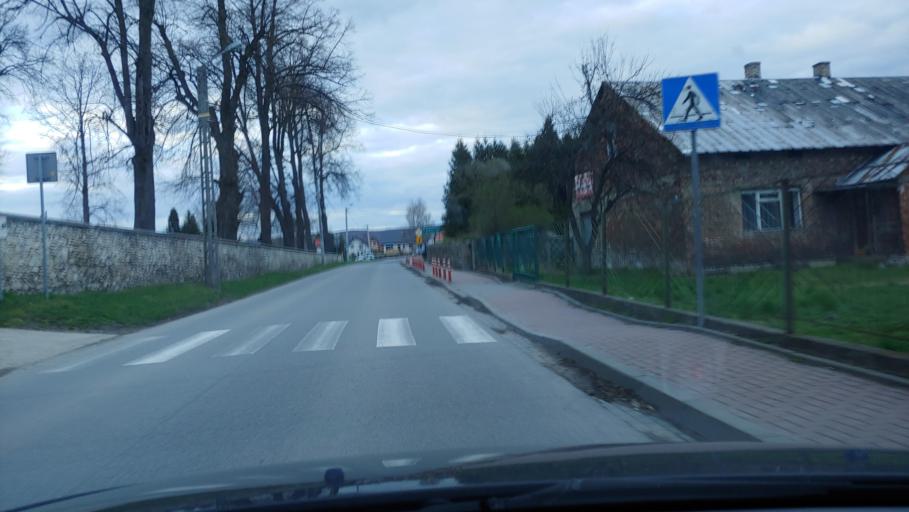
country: PL
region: Lesser Poland Voivodeship
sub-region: Powiat krakowski
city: Rudawa
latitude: 50.1239
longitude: 19.7129
